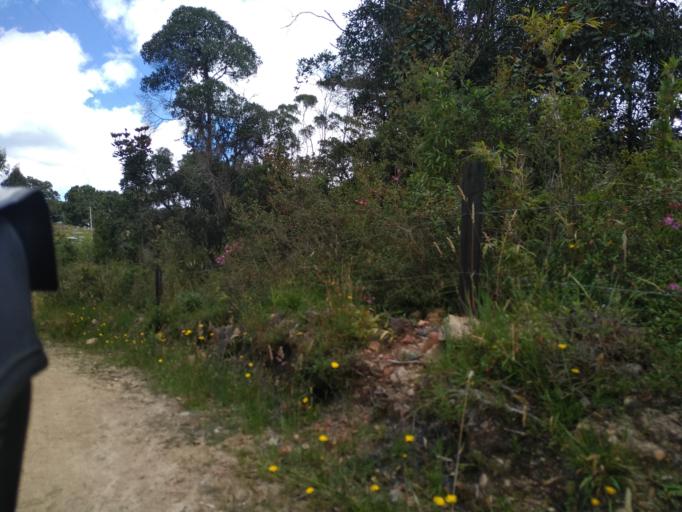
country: CO
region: Boyaca
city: Duitama
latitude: 5.9397
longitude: -73.1184
